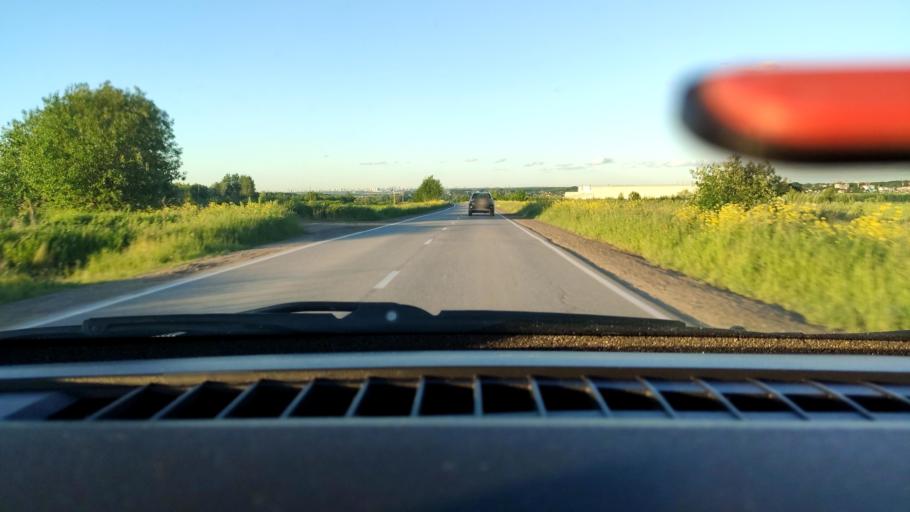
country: RU
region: Perm
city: Kultayevo
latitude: 57.9251
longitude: 55.9732
